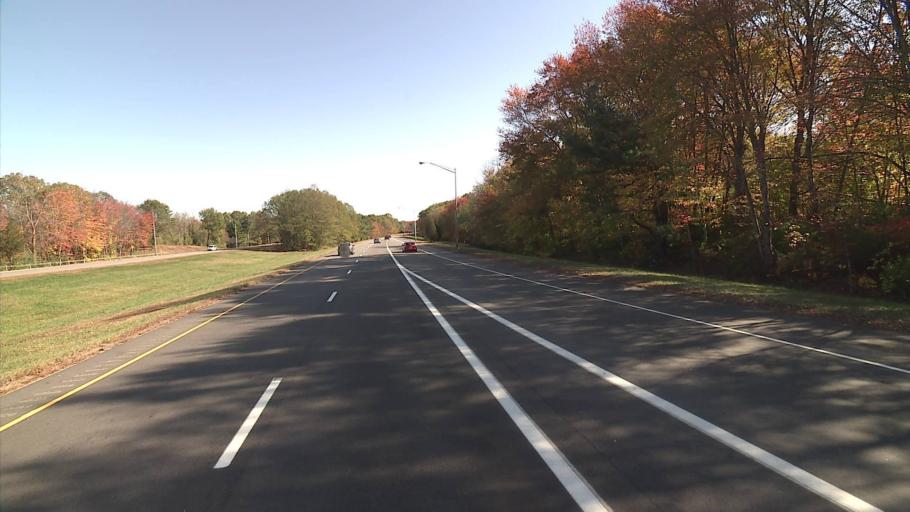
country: US
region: Connecticut
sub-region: Windham County
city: Willimantic
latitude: 41.7275
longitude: -72.2373
